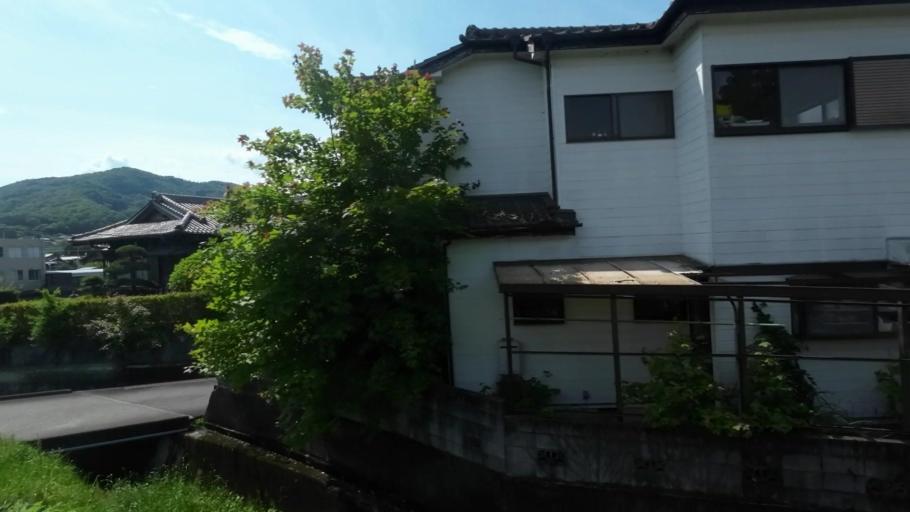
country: JP
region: Tokushima
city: Wakimachi
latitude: 34.0547
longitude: 134.2322
